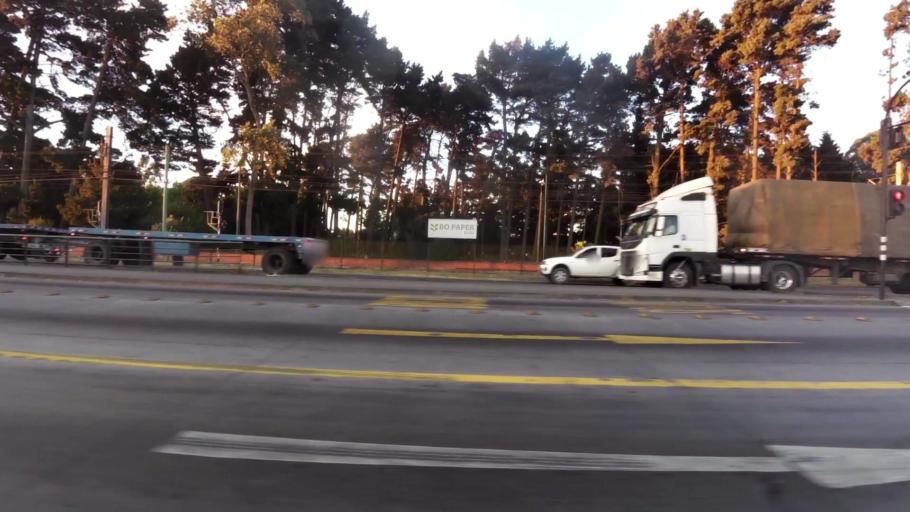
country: CL
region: Biobio
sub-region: Provincia de Concepcion
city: Concepcion
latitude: -36.8387
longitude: -73.0957
